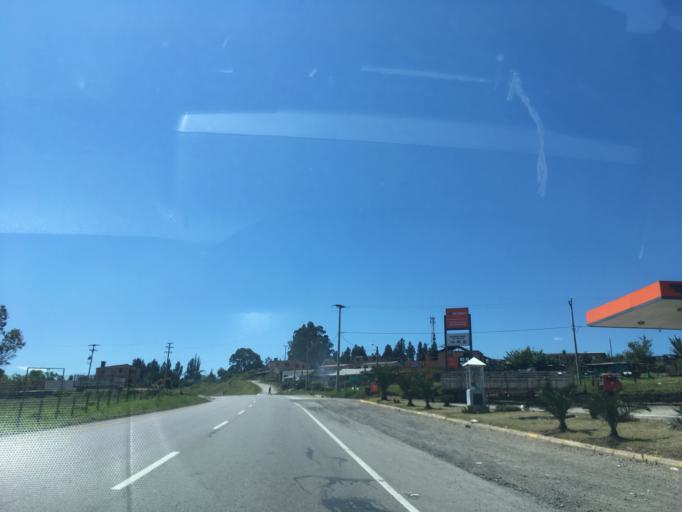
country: CO
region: Boyaca
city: Tuta
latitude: 5.7242
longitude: -73.2255
